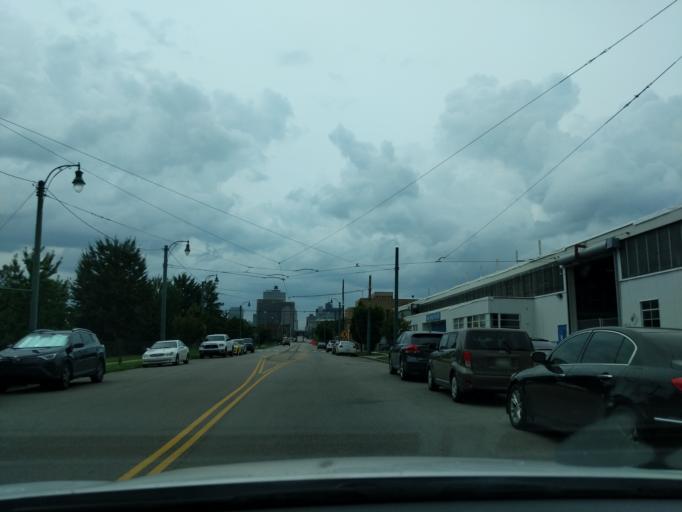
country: US
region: Tennessee
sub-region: Shelby County
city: Memphis
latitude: 35.1600
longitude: -90.0469
